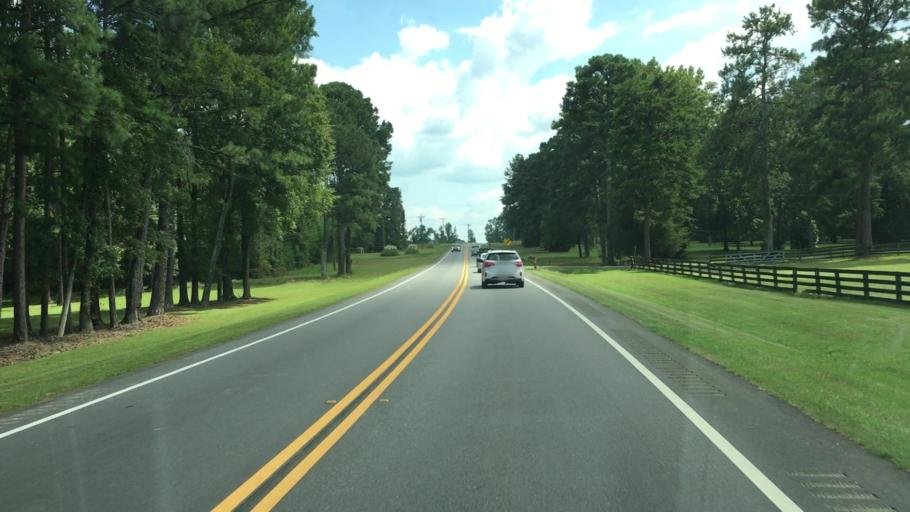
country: US
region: Georgia
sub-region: Putnam County
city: Eatonton
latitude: 33.3782
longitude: -83.3801
